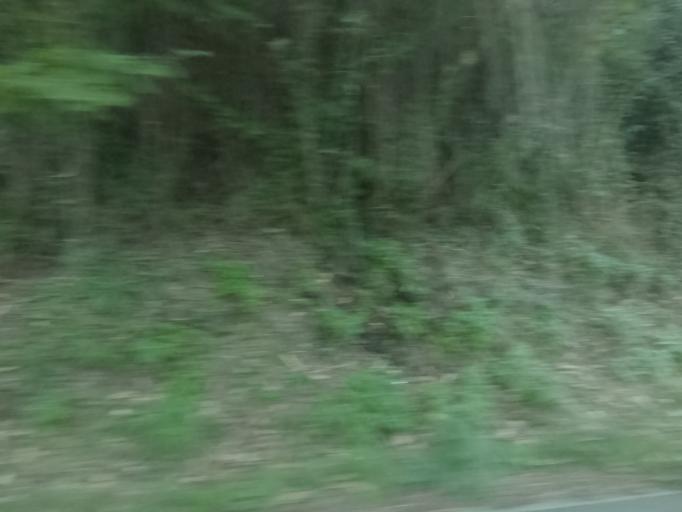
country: PT
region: Vila Real
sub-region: Mesao Frio
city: Mesao Frio
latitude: 41.1849
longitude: -7.8614
